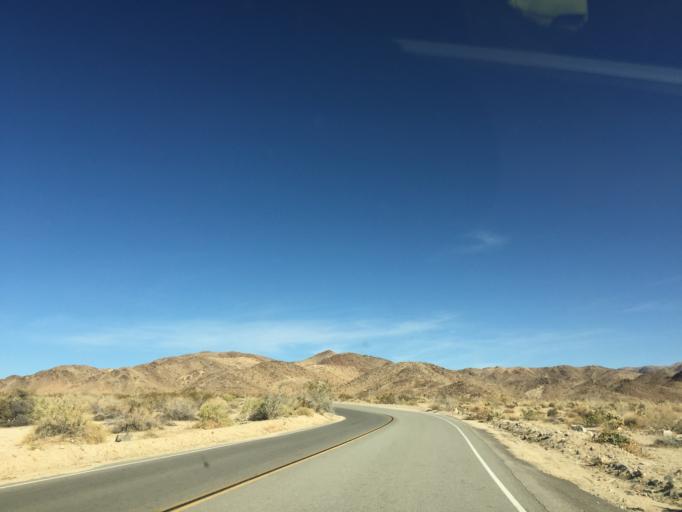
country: US
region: California
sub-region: San Bernardino County
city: Twentynine Palms
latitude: 33.9310
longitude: -115.9479
